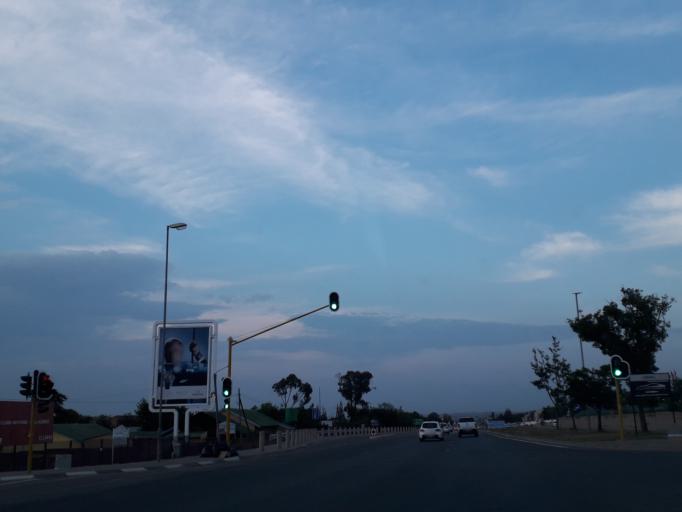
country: ZA
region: Gauteng
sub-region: City of Johannesburg Metropolitan Municipality
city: Diepsloot
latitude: -26.0124
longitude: 28.0110
